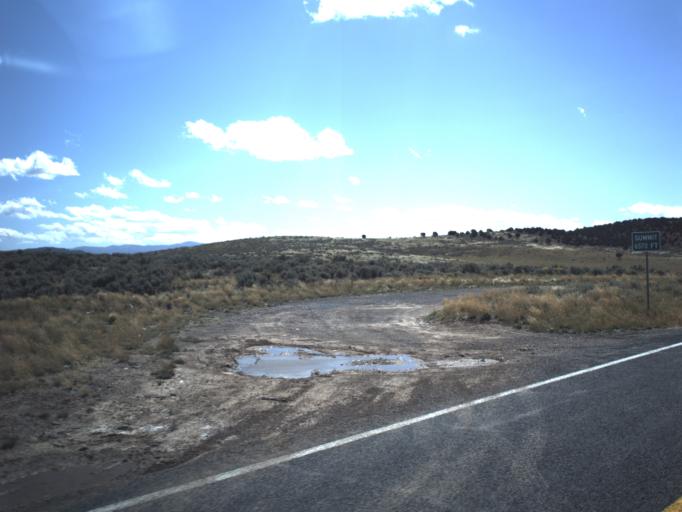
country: US
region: Utah
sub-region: Iron County
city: Parowan
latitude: 38.0681
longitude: -112.9618
